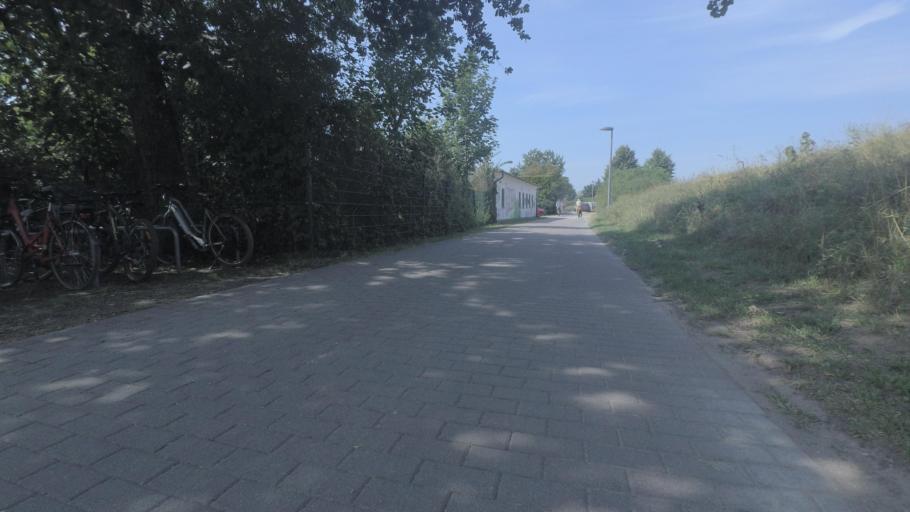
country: DE
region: Mecklenburg-Vorpommern
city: Waren
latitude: 53.5185
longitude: 12.6667
